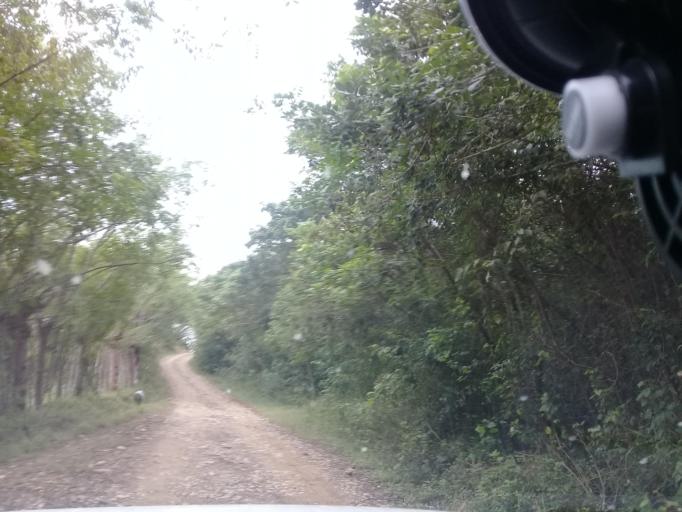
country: MX
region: Hidalgo
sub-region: Huejutla de Reyes
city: Chalahuiyapa
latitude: 21.1667
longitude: -98.3453
